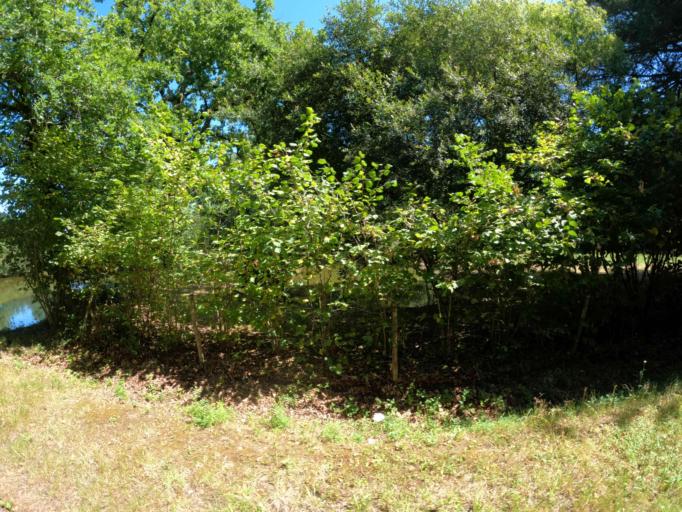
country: FR
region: Pays de la Loire
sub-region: Departement de la Loire-Atlantique
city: La Limouziniere
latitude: 46.9412
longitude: -1.6232
